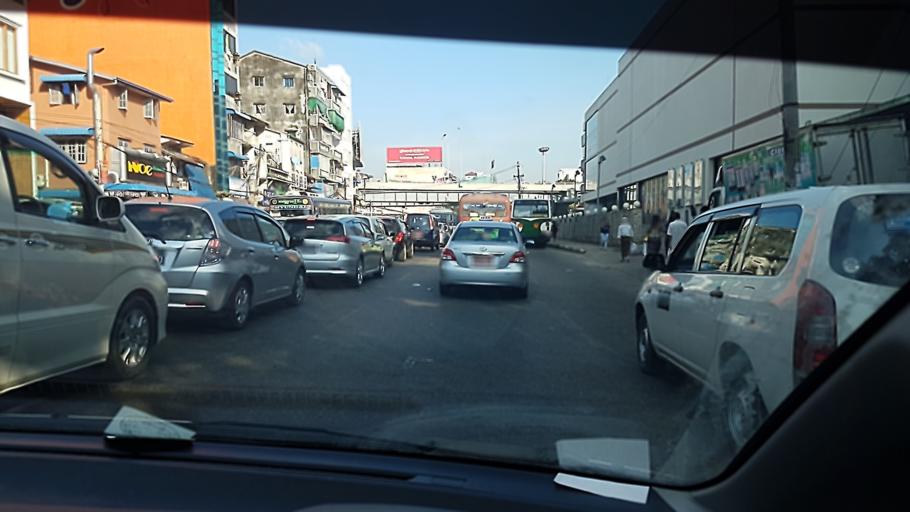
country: MM
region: Yangon
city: Yangon
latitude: 16.8115
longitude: 96.1698
